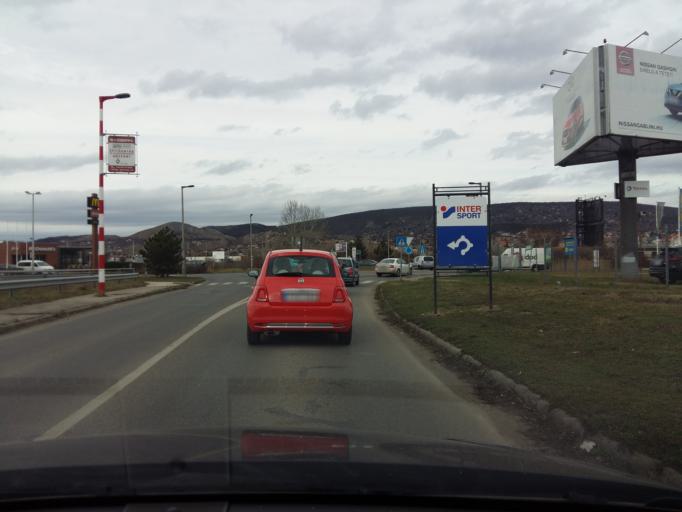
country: HU
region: Pest
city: Budaors
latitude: 47.4516
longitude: 18.9695
